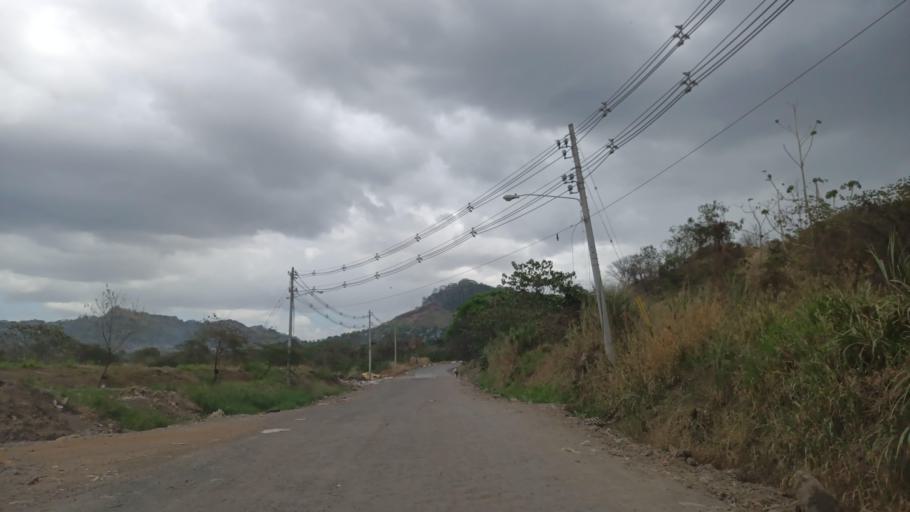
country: PA
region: Panama
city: Las Cumbres
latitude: 9.0534
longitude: -79.5648
